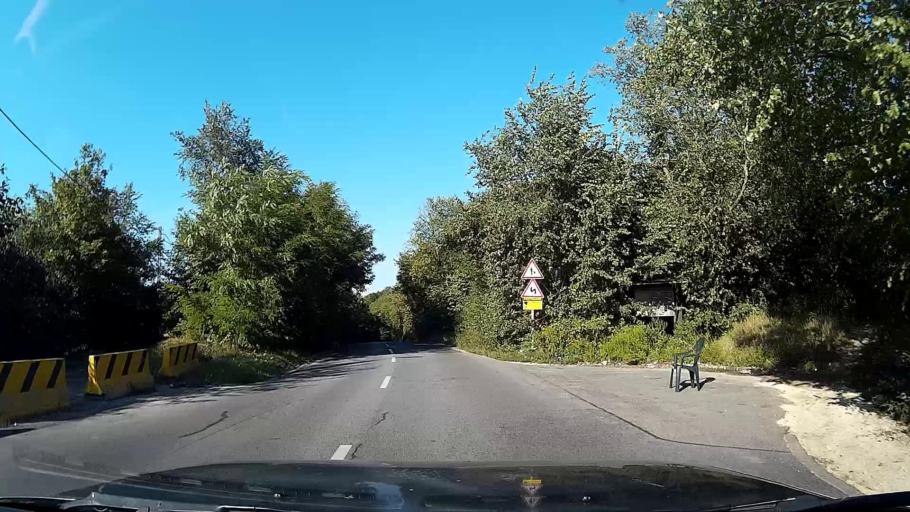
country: HU
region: Pest
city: Diosd
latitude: 47.4278
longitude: 18.9800
